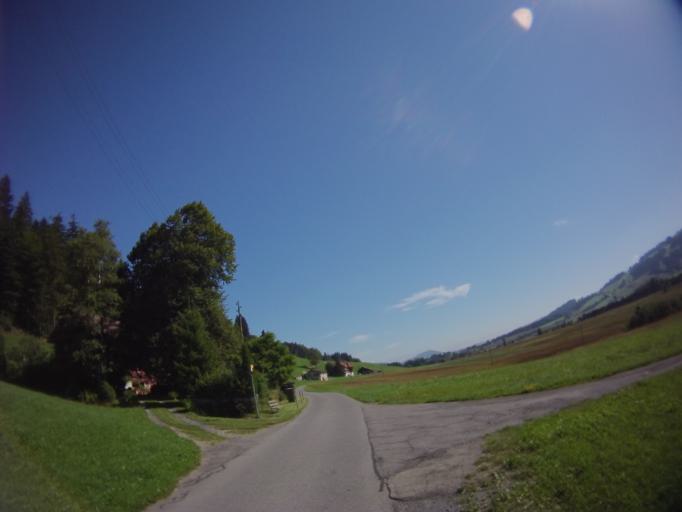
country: CH
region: Schwyz
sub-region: Bezirk Schwyz
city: Rothenthurm
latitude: 47.1296
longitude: 8.6738
